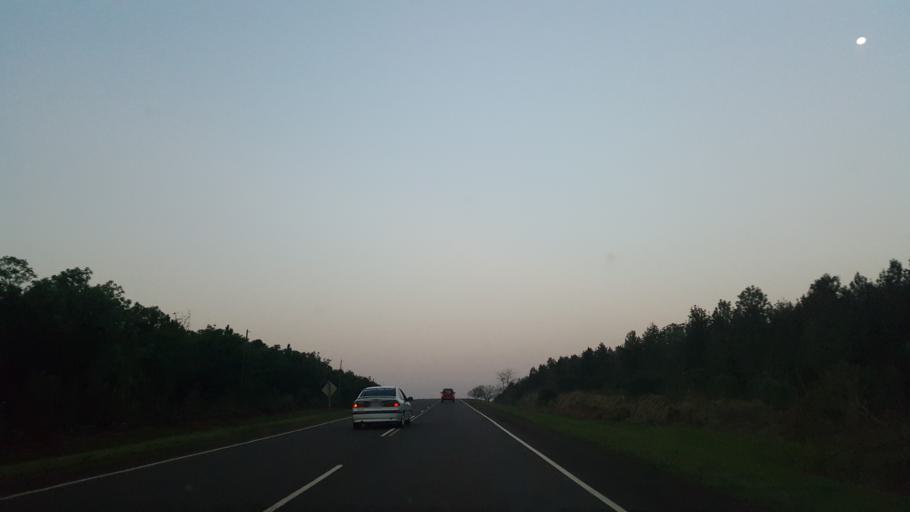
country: AR
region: Misiones
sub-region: Departamento de Capital
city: Posadas
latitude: -27.4387
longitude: -56.0196
